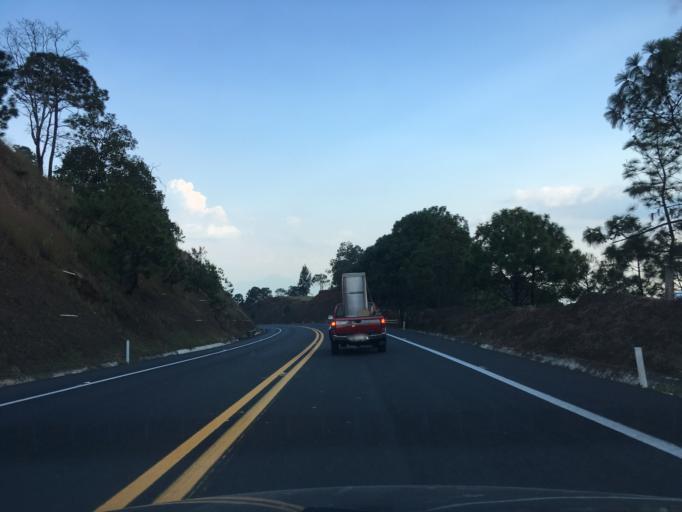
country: MX
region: Michoacan
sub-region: Uruapan
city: Toreo Bajo (El Toreo Bajo)
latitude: 19.4169
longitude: -101.9826
